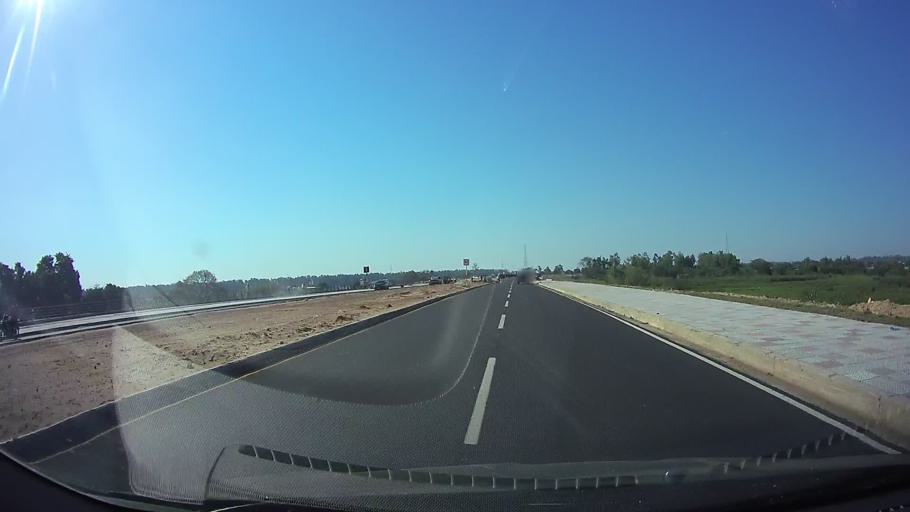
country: PY
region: Asuncion
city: Asuncion
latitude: -25.2541
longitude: -57.6066
